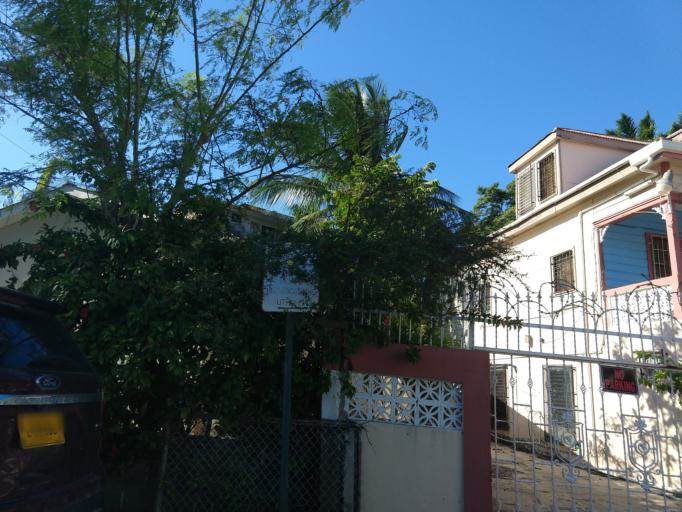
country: BZ
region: Belize
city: Belize City
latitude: 17.4962
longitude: -88.1839
